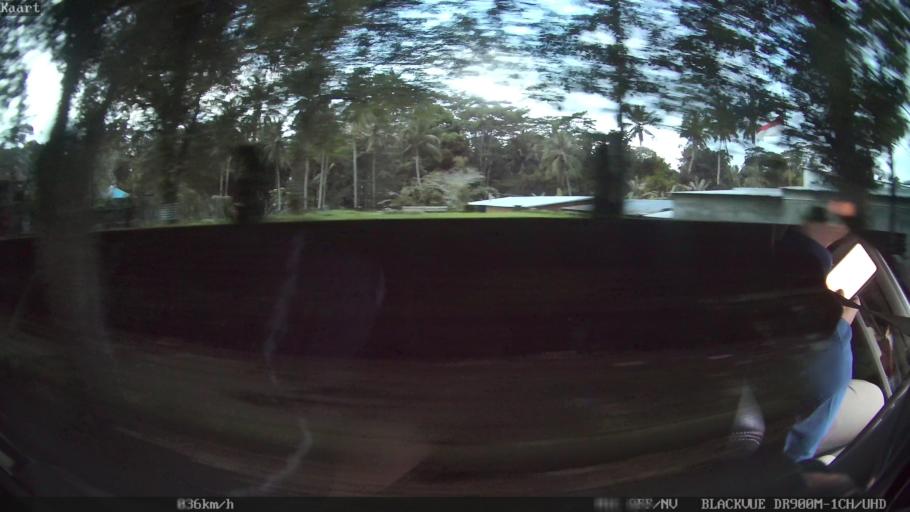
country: ID
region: Bali
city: Bunutan
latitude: -8.4802
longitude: 115.2475
